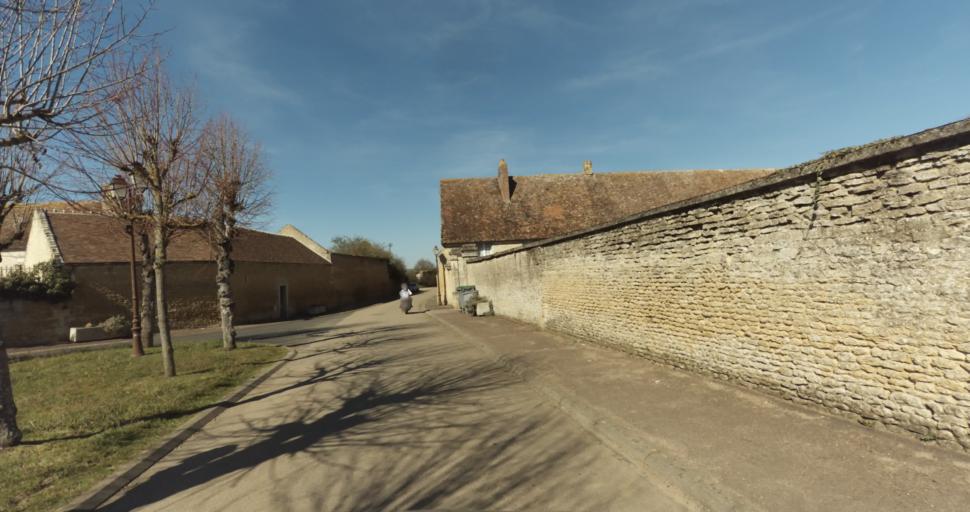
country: FR
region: Lower Normandy
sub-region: Departement du Calvados
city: Saint-Pierre-sur-Dives
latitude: 49.0366
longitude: -0.0265
